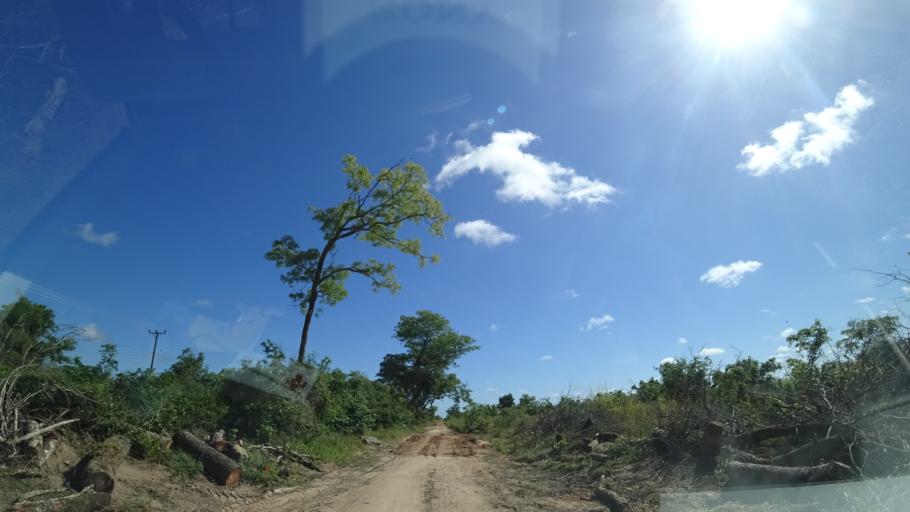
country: MZ
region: Sofala
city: Dondo
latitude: -19.2841
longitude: 34.6856
